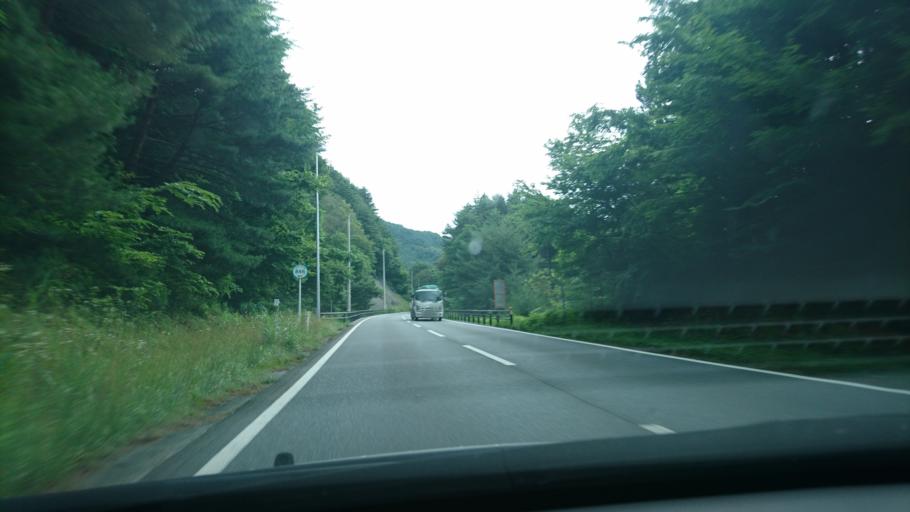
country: JP
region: Iwate
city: Kamaishi
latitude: 39.1602
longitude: 141.8494
